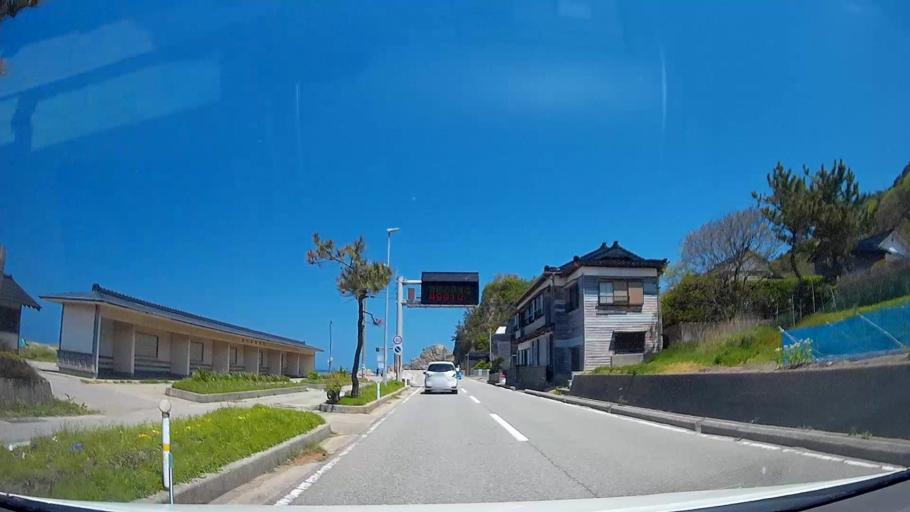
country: JP
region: Ishikawa
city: Nanao
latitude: 37.4548
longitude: 137.0737
